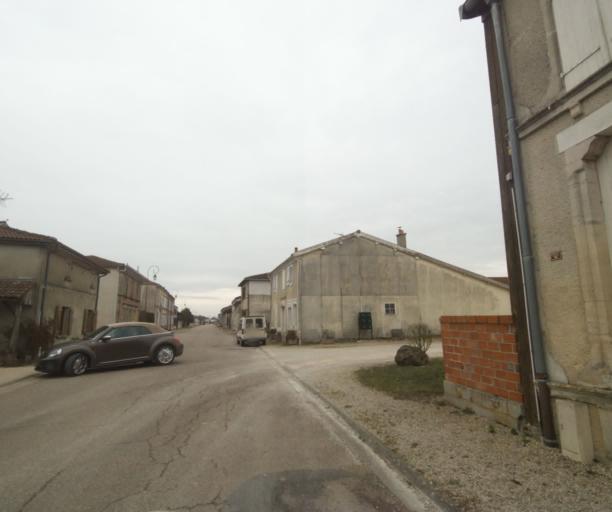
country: FR
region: Champagne-Ardenne
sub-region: Departement de la Haute-Marne
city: Villiers-en-Lieu
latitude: 48.6378
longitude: 4.7691
